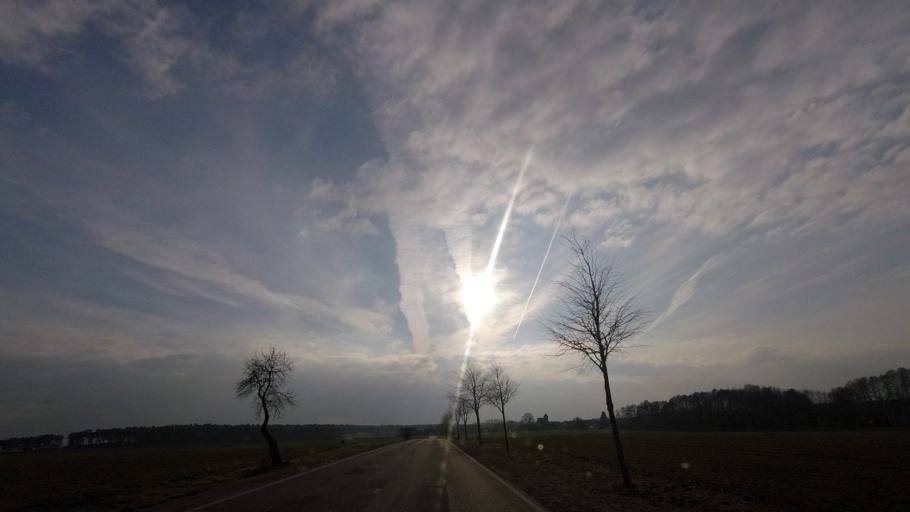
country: DE
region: Brandenburg
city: Belzig
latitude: 52.1404
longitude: 12.6487
